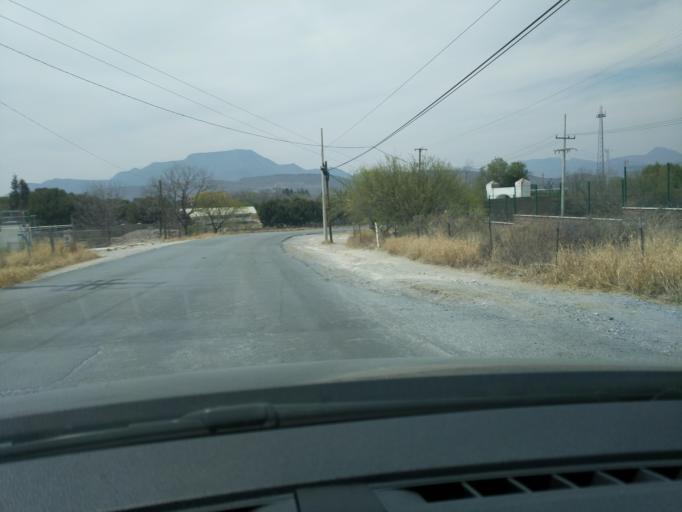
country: MX
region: Coahuila
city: Saltillo
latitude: 25.3530
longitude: -101.0247
